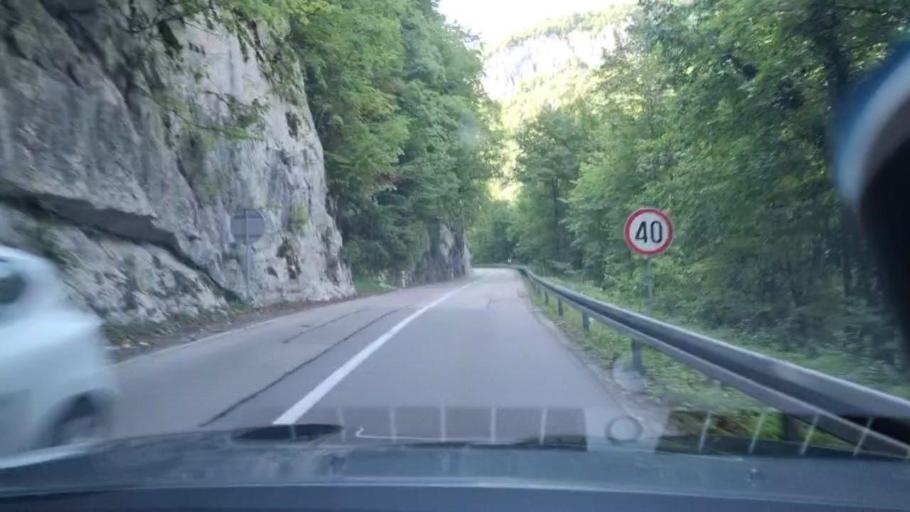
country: BA
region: Federation of Bosnia and Herzegovina
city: Bosanska Krupa
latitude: 44.8693
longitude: 16.0873
